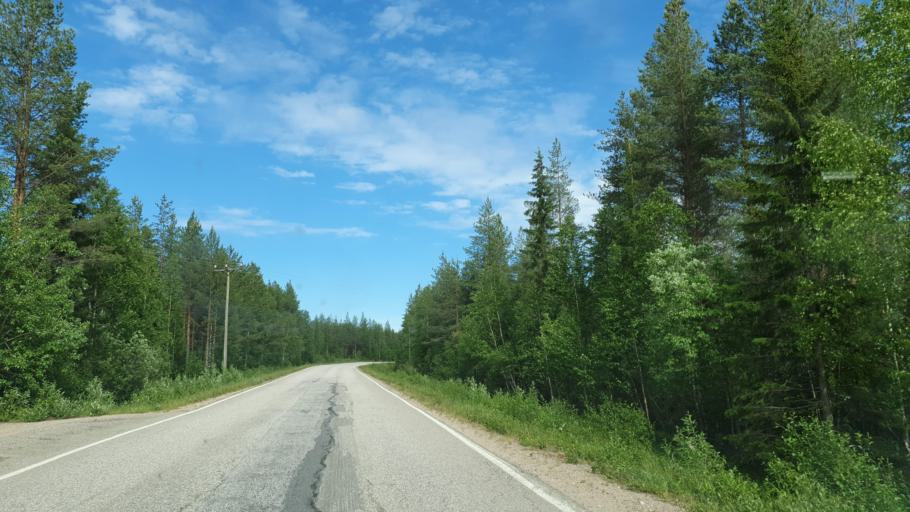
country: FI
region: Kainuu
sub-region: Kehys-Kainuu
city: Suomussalmi
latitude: 64.5927
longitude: 29.0862
